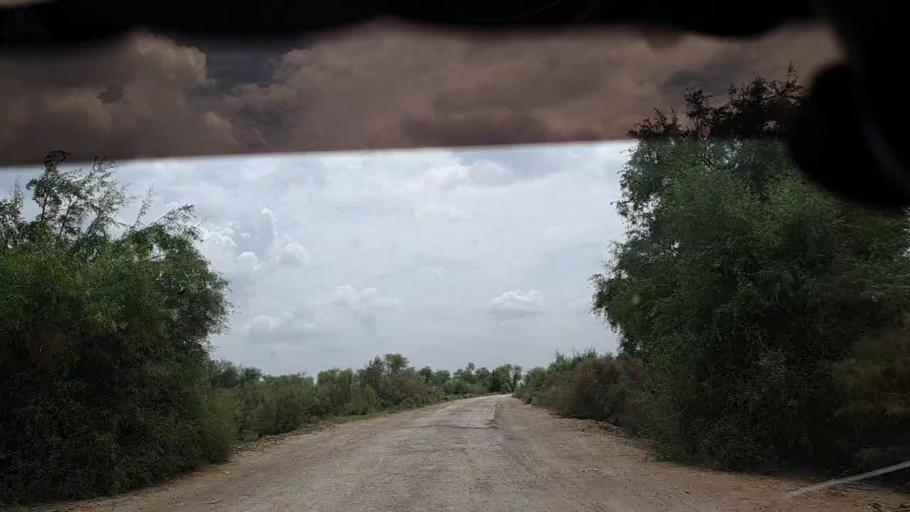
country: PK
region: Sindh
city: Ghauspur
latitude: 28.0617
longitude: 68.9404
